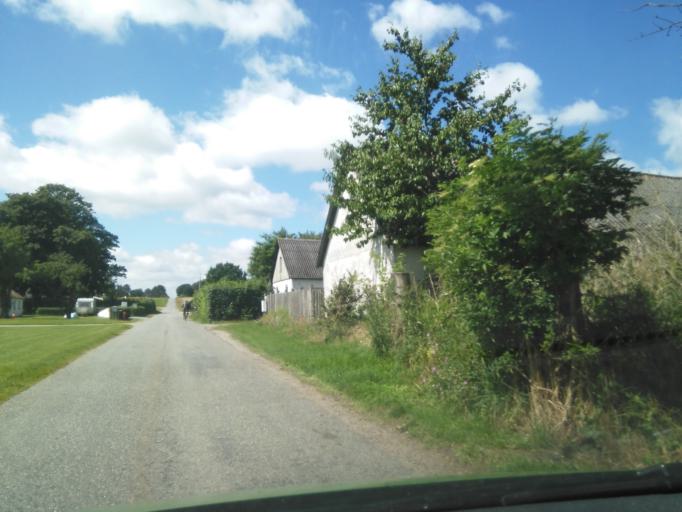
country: DK
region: Central Jutland
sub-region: Arhus Kommune
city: Logten
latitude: 56.1976
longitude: 10.3872
